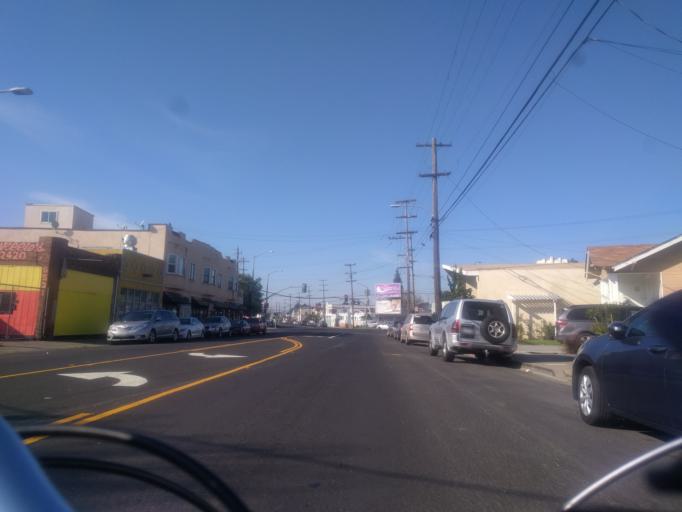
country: US
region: California
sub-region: Alameda County
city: Alameda
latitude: 37.7727
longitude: -122.1948
